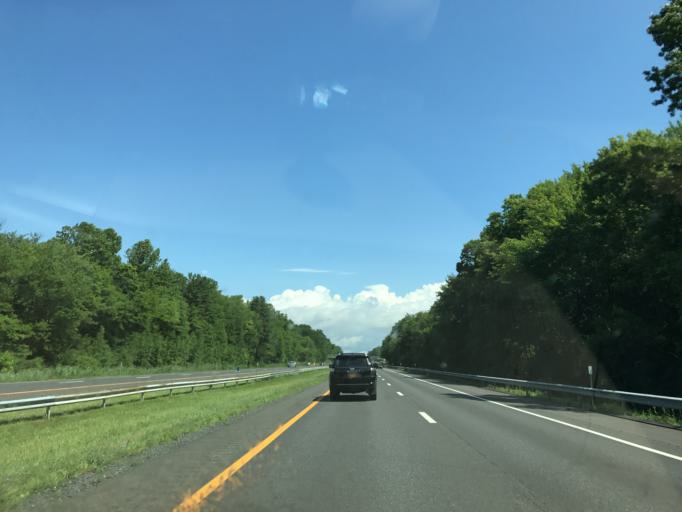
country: US
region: New York
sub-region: Ulster County
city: Tillson
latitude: 41.8257
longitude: -74.0572
